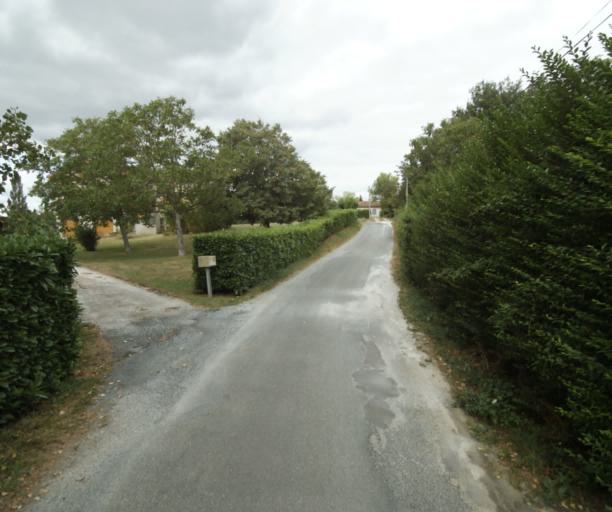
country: FR
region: Midi-Pyrenees
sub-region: Departement du Tarn
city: Soreze
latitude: 43.4556
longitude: 2.0703
